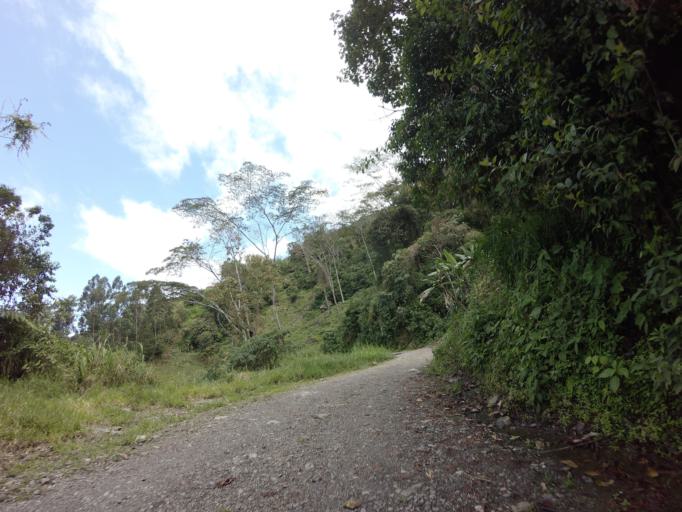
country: CO
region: Caldas
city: Pensilvania
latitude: 5.4564
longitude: -75.1737
